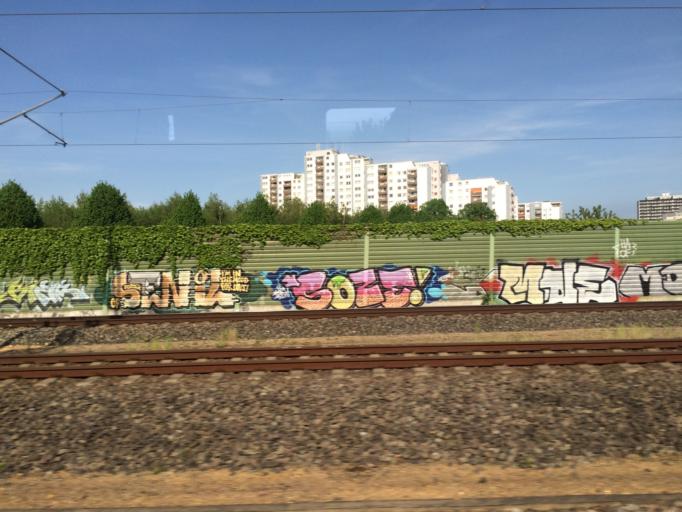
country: DE
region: North Rhine-Westphalia
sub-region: Regierungsbezirk Koln
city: Gremberghoven
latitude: 50.8975
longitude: 7.0560
